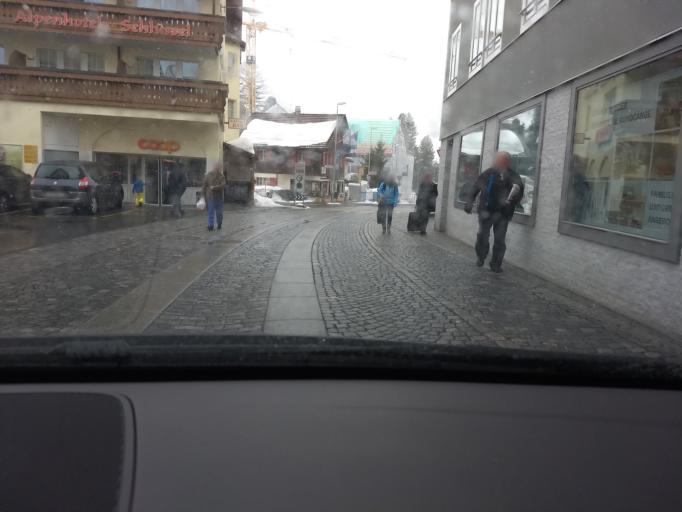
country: CH
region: Uri
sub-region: Uri
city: Andermatt
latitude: 46.6344
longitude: 8.5968
